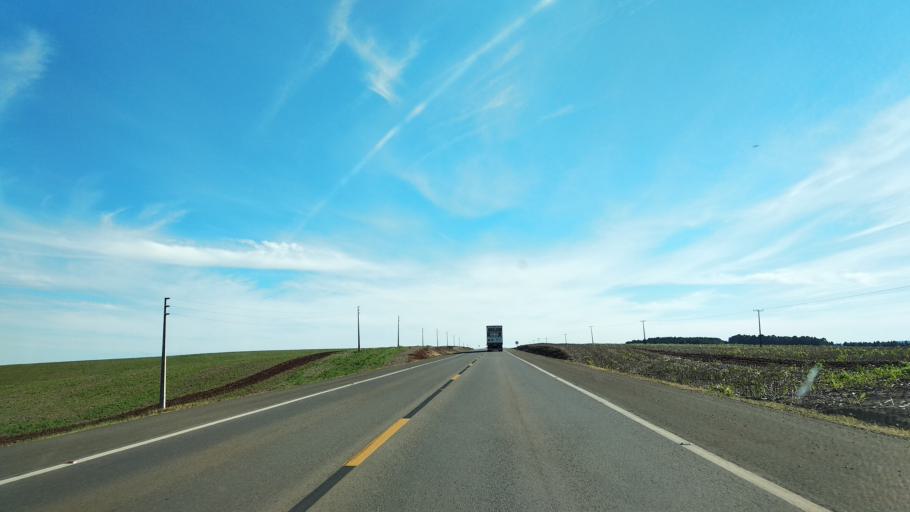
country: BR
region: Santa Catarina
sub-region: Campos Novos
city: Campos Novos
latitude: -27.4873
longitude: -51.3212
